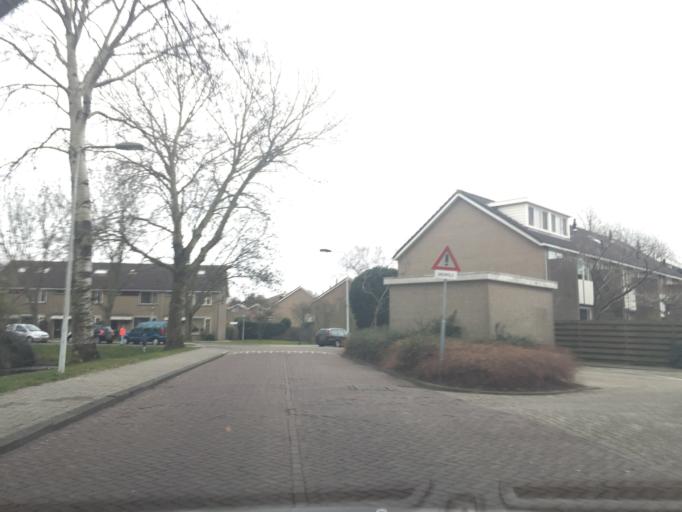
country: NL
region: South Holland
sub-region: Gemeente Leiden
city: Leiden
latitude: 52.1822
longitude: 4.5003
